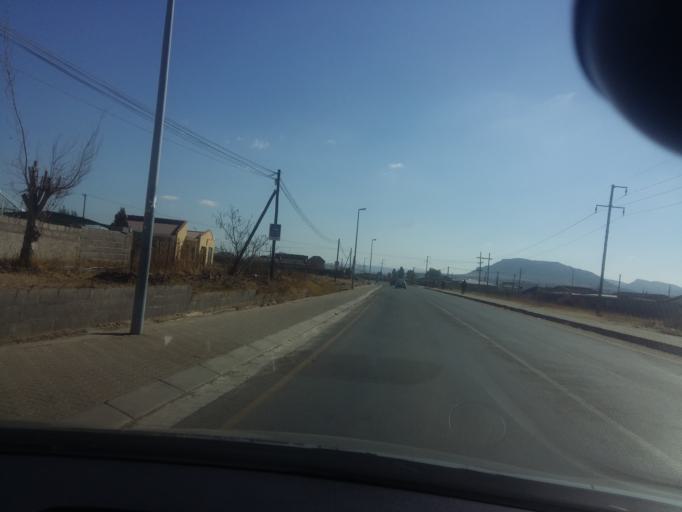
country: LS
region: Maseru
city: Maseru
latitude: -29.3423
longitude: 27.4510
